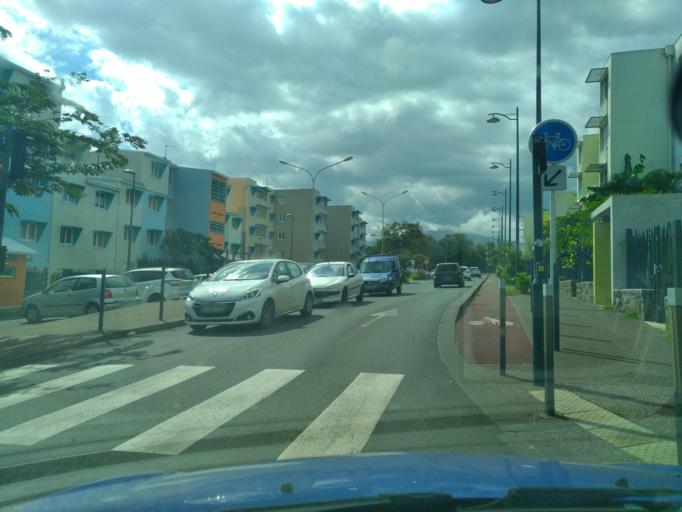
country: RE
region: Reunion
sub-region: Reunion
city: Saint-Pierre
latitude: -21.3363
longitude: 55.4637
